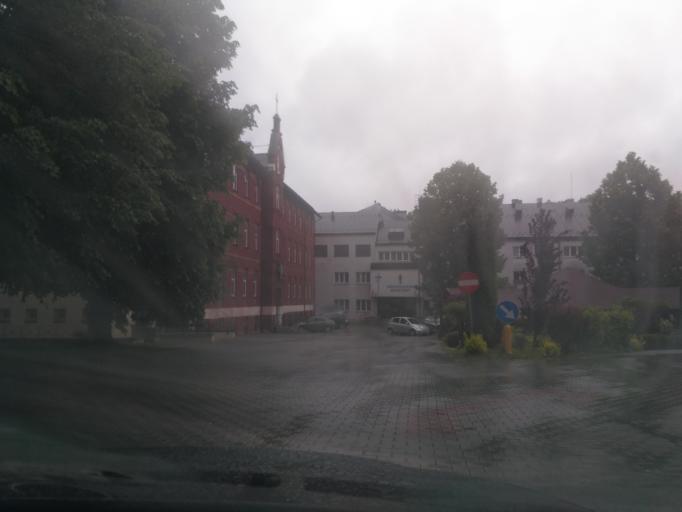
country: PL
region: Subcarpathian Voivodeship
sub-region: Powiat jasielski
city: Debowiec
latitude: 49.6837
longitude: 21.4653
